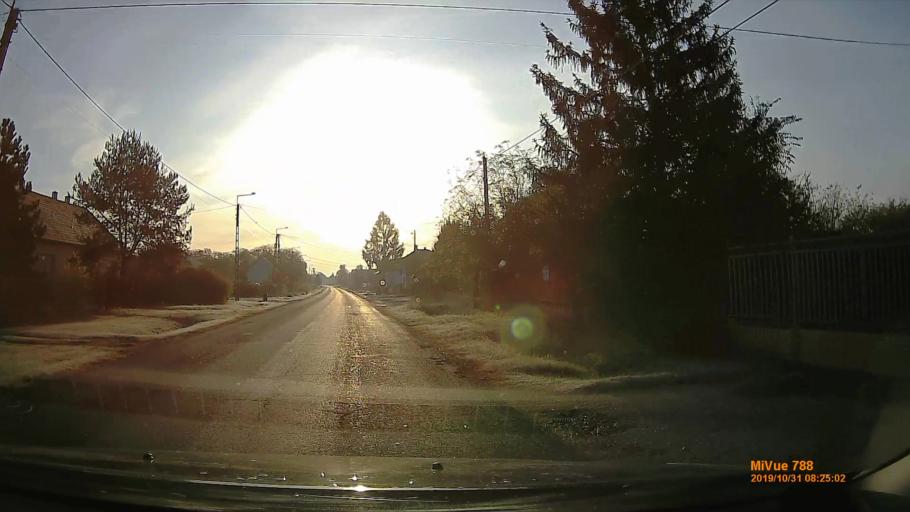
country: HU
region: Pest
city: Tapiobicske
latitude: 47.3674
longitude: 19.6652
